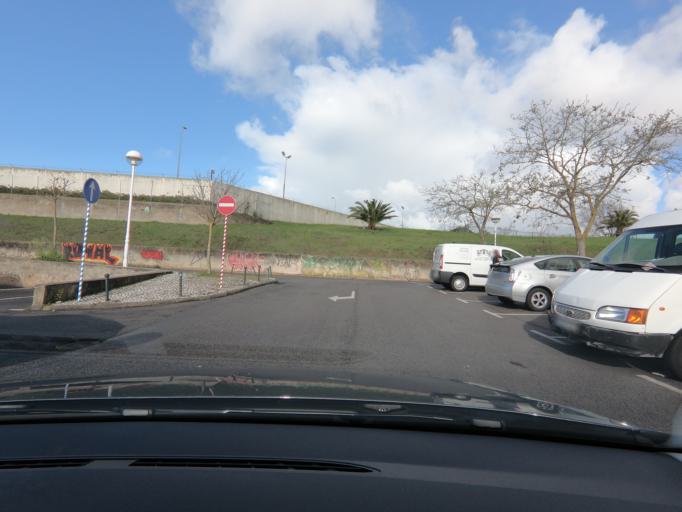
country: PT
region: Lisbon
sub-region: Oeiras
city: Carcavelos
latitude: 38.6811
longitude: -9.3205
